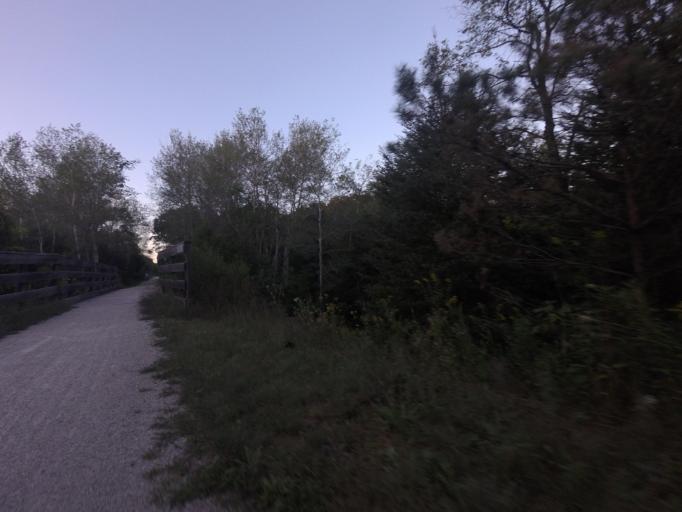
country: CA
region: Ontario
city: Orangeville
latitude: 43.9381
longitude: -79.8423
